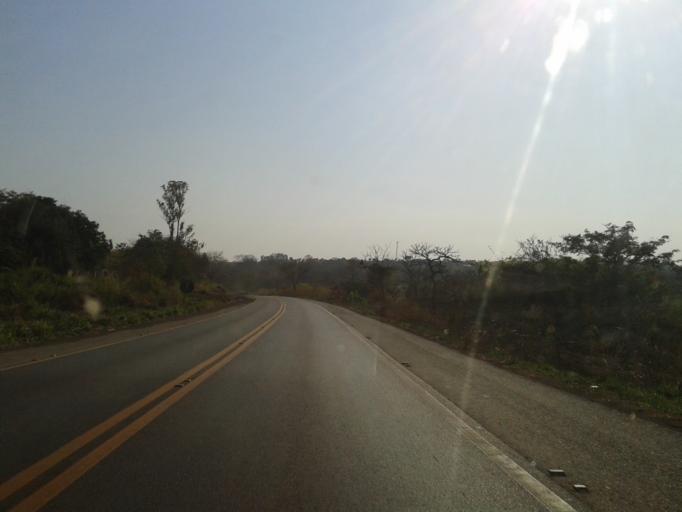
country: BR
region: Minas Gerais
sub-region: Ituiutaba
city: Ituiutaba
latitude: -18.9614
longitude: -49.4731
